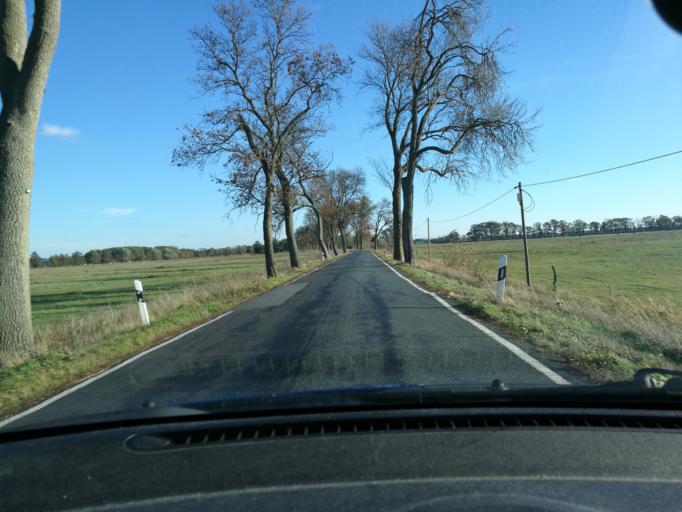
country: DE
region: Brandenburg
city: Lenzen
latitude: 53.1107
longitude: 11.4069
